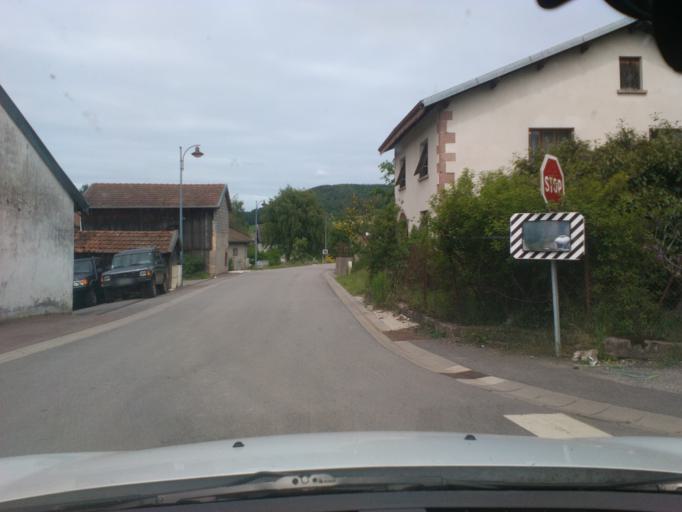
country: FR
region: Lorraine
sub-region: Departement des Vosges
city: Le Tholy
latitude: 48.1349
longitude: 6.7052
